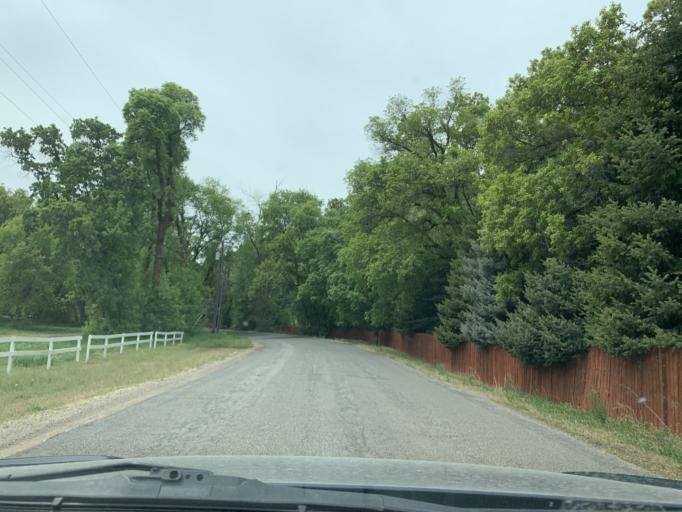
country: US
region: Utah
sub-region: Utah County
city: Mapleton
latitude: 40.1663
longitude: -111.4967
